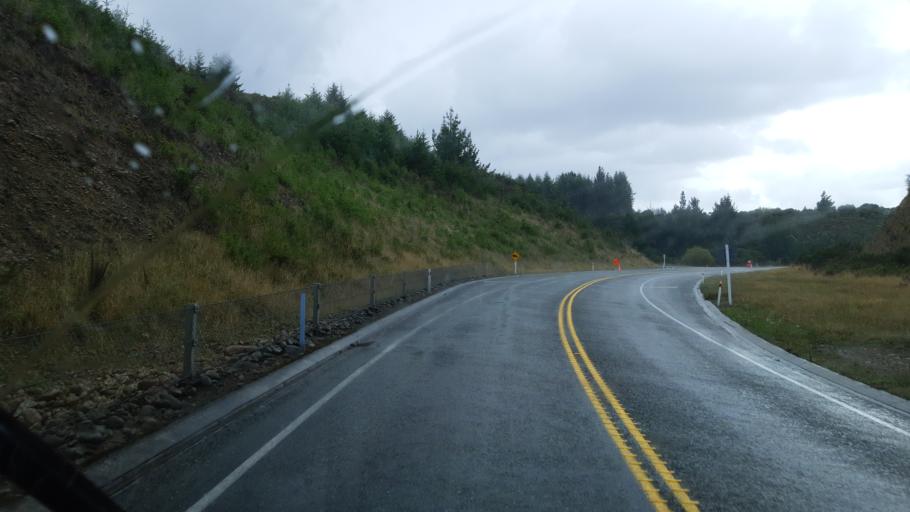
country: NZ
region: Tasman
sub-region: Tasman District
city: Wakefield
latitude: -41.4808
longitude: 172.9070
